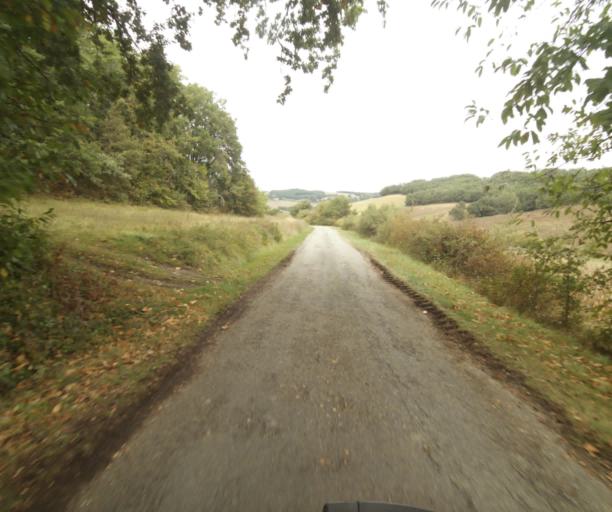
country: FR
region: Midi-Pyrenees
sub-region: Departement du Tarn-et-Garonne
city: Beaumont-de-Lomagne
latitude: 43.8438
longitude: 1.0919
